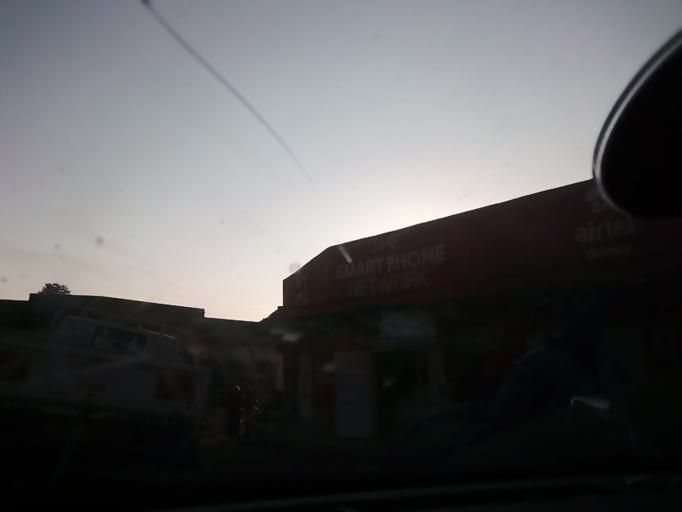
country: UG
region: Central Region
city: Masaka
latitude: -0.3206
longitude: 31.7590
